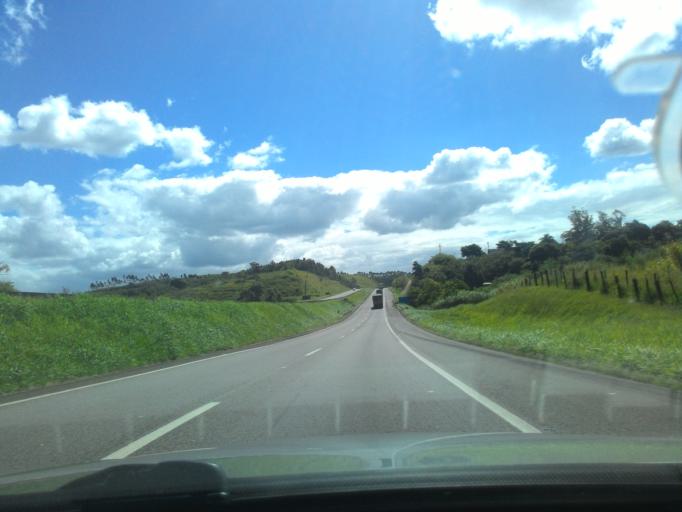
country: BR
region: Sao Paulo
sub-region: Cajati
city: Cajati
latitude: -24.7412
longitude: -48.1265
